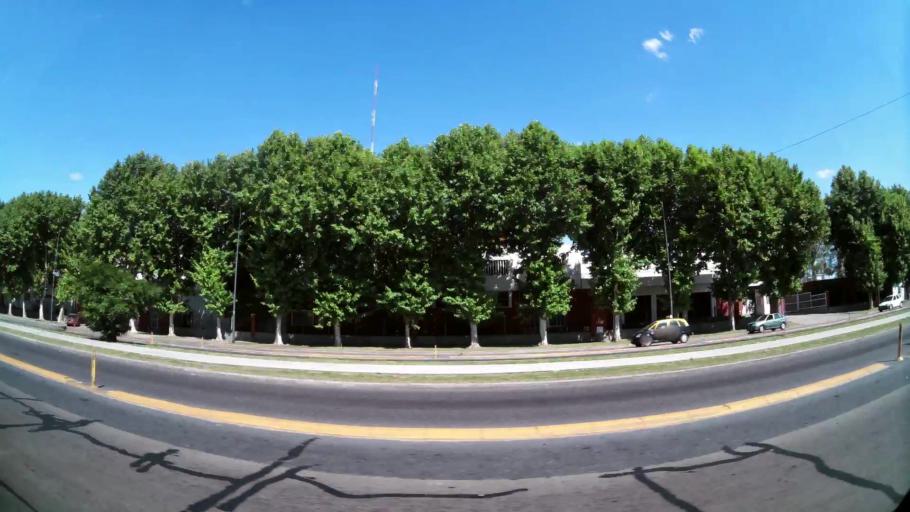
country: AR
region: Buenos Aires F.D.
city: Villa Lugano
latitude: -34.6927
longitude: -58.4644
